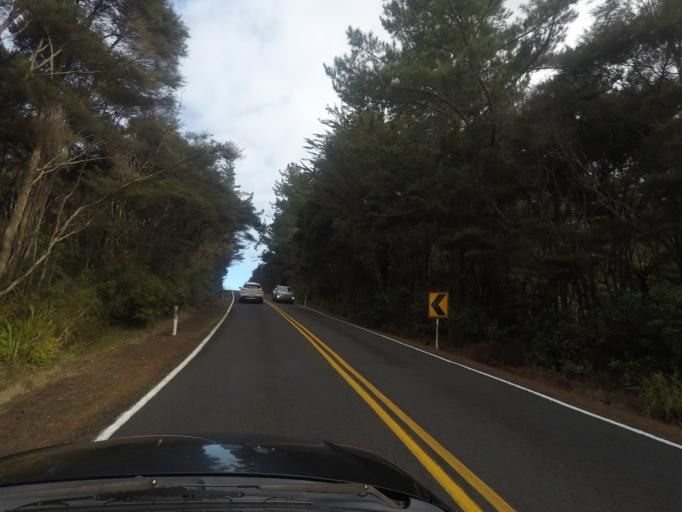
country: NZ
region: Auckland
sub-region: Auckland
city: Titirangi
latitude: -37.0007
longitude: 174.5874
